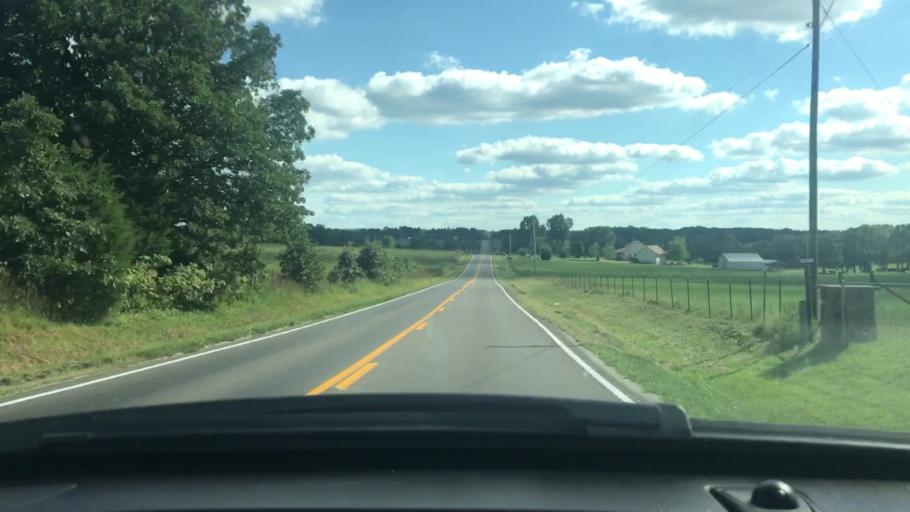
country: US
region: Missouri
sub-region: Wright County
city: Mountain Grove
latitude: 37.2463
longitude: -92.3003
